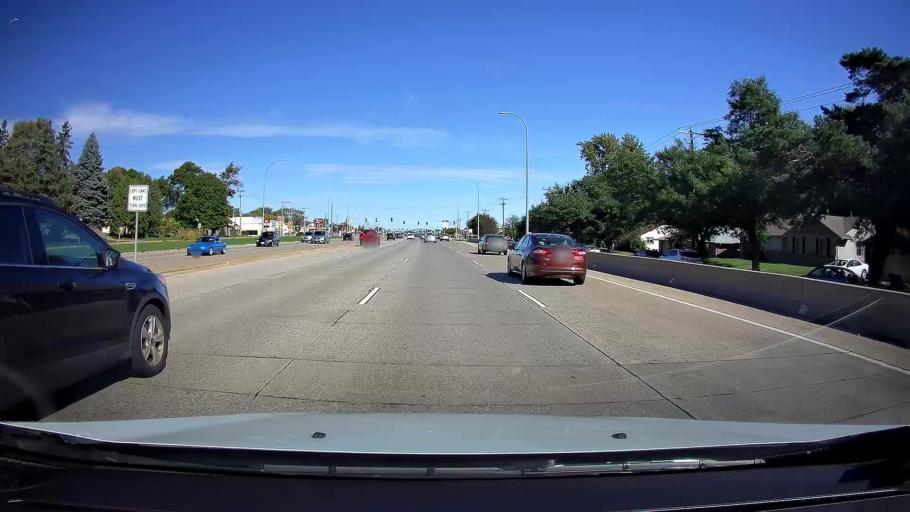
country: US
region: Minnesota
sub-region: Ramsey County
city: Falcon Heights
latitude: 45.0015
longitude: -93.1664
